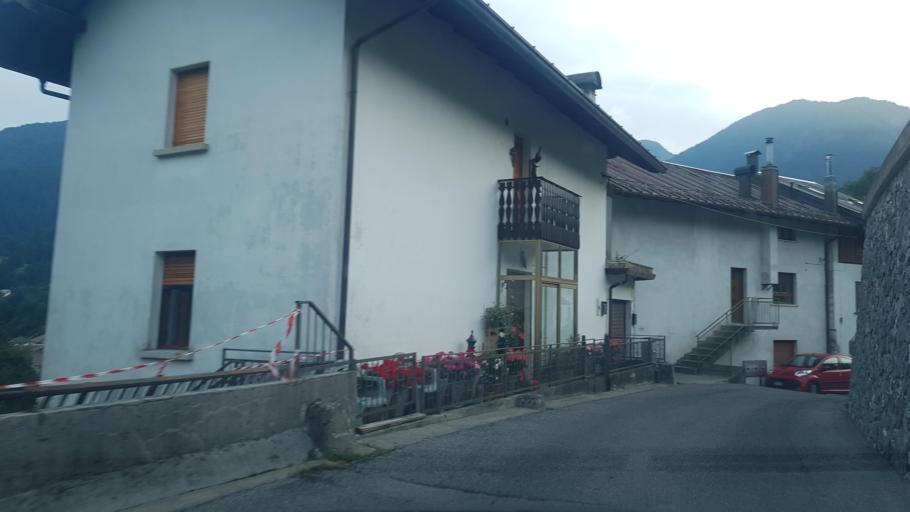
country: IT
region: Friuli Venezia Giulia
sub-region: Provincia di Udine
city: Paularo
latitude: 46.5350
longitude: 13.1171
